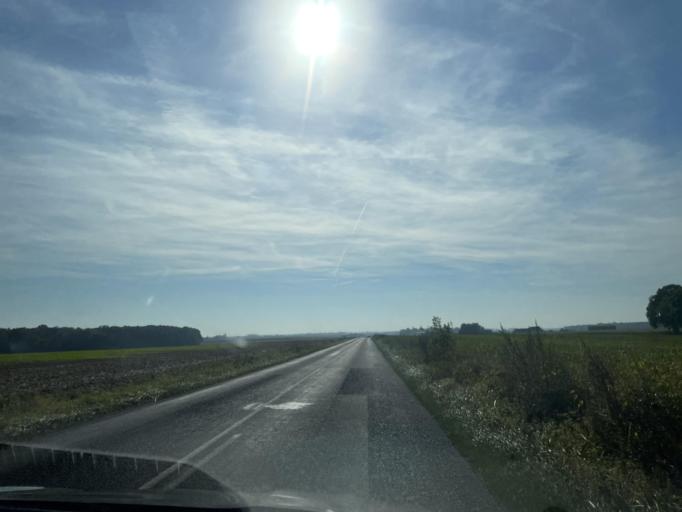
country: FR
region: Ile-de-France
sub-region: Departement de Seine-et-Marne
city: Sammeron
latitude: 48.8911
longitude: 3.0660
